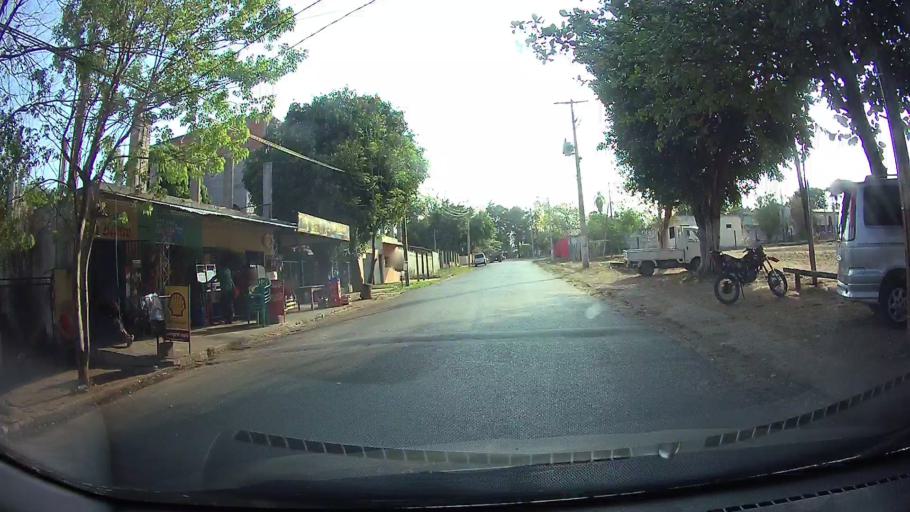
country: PY
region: Central
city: Limpio
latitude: -25.2018
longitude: -57.5064
